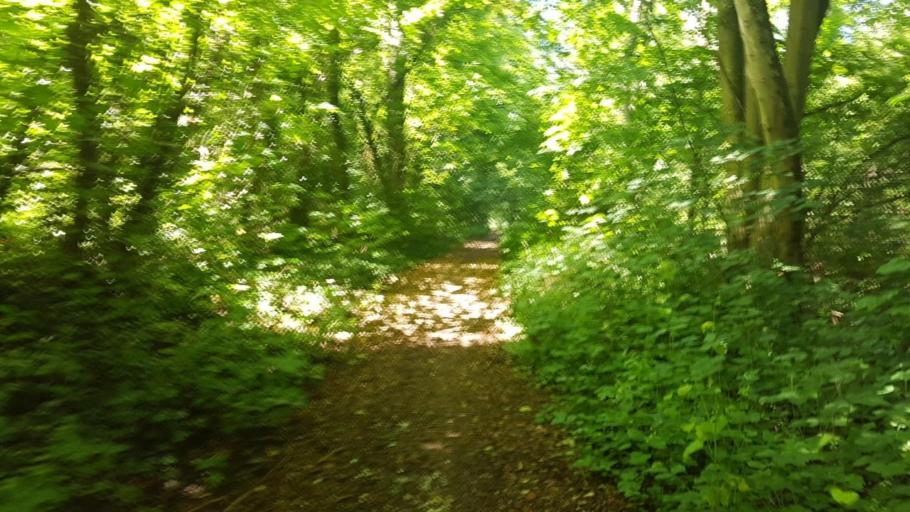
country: FR
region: Ile-de-France
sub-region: Departement de Seine-et-Marne
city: Nanteuil-les-Meaux
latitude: 48.9357
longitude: 2.8938
